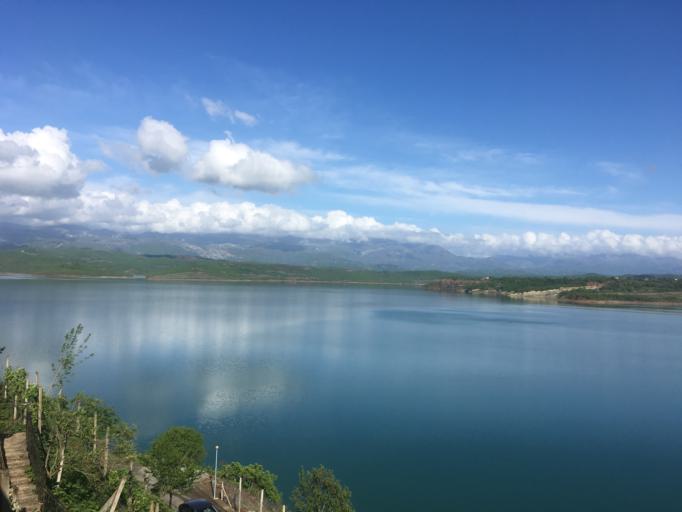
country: AL
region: Diber
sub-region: Rrethi i Matit
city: Ulez
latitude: 41.6920
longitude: 19.8322
